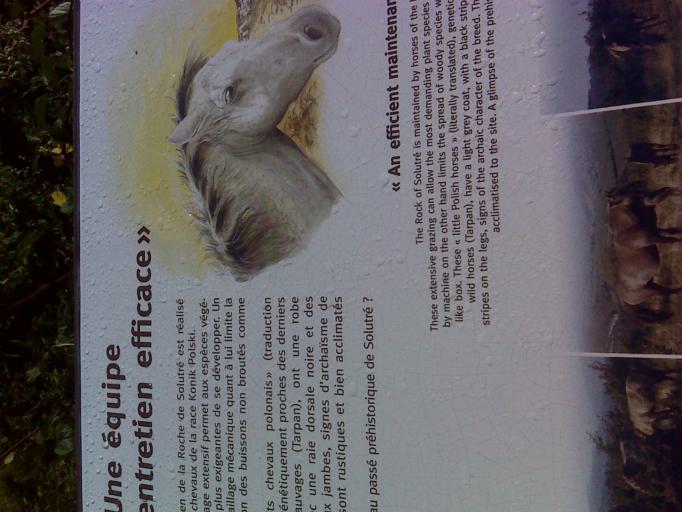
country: FR
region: Bourgogne
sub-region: Departement de Saone-et-Loire
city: Prisse
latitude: 46.3009
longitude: 4.7237
